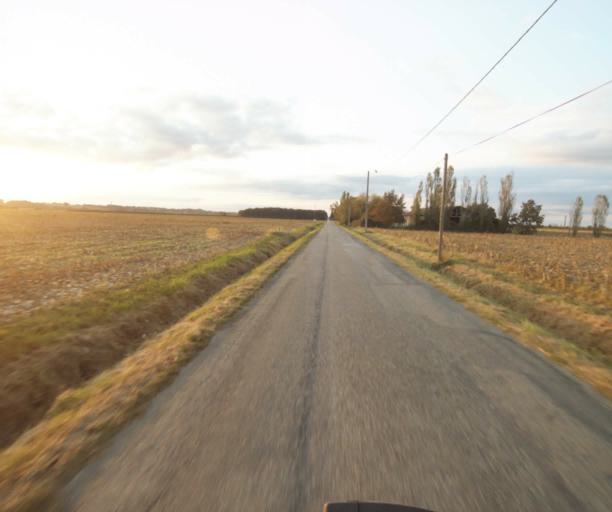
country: FR
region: Midi-Pyrenees
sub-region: Departement du Tarn-et-Garonne
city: Verdun-sur-Garonne
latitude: 43.8248
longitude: 1.2370
